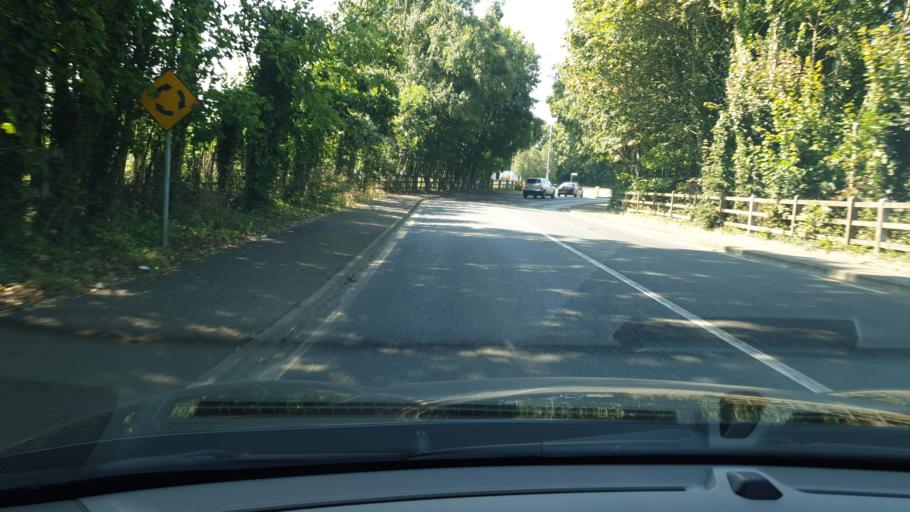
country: IE
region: Leinster
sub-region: An Mhi
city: Trim
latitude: 53.5466
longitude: -6.7928
